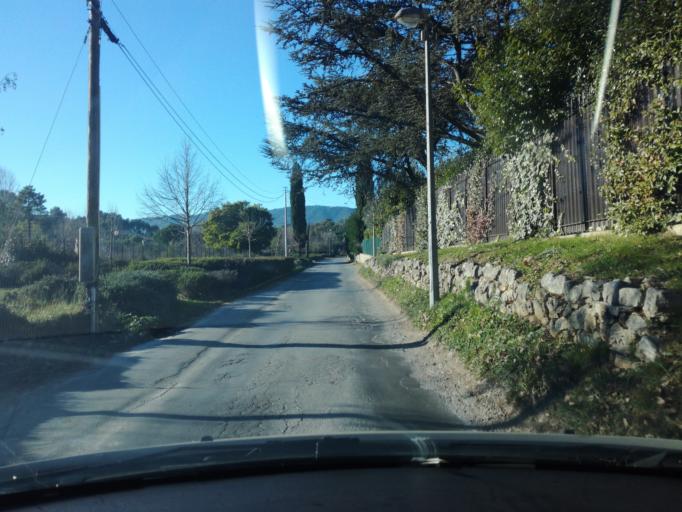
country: FR
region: Provence-Alpes-Cote d'Azur
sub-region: Departement des Alpes-Maritimes
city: La Roquette-sur-Siagne
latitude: 43.6013
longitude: 6.9502
